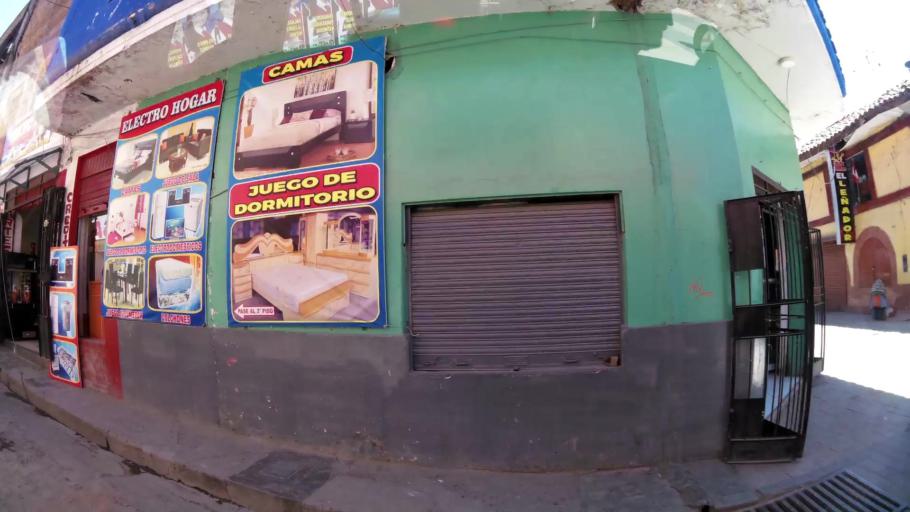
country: PE
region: Junin
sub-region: Provincia de Jauja
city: Jauja
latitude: -11.7771
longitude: -75.4988
